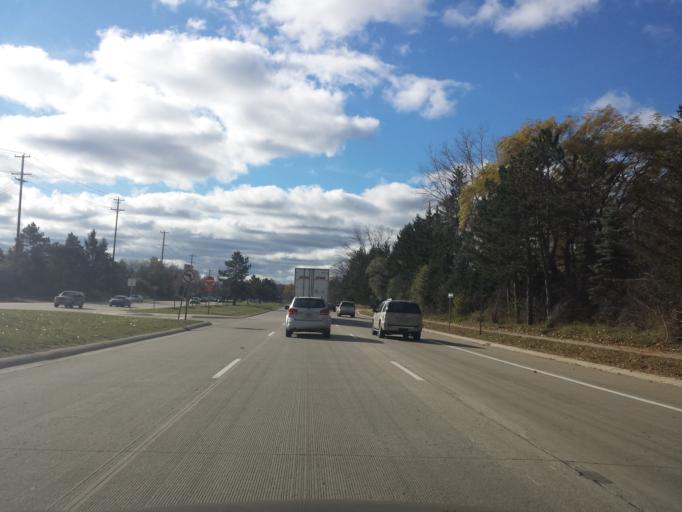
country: US
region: Michigan
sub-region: Oakland County
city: Bloomfield Hills
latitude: 42.5652
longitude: -83.2832
